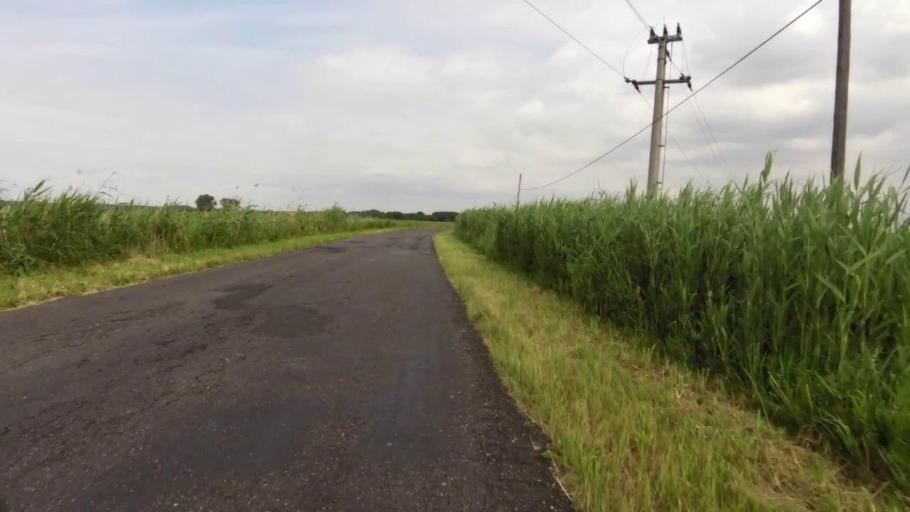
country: PL
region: West Pomeranian Voivodeship
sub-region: Powiat goleniowski
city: Stepnica
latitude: 53.6758
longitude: 14.5572
